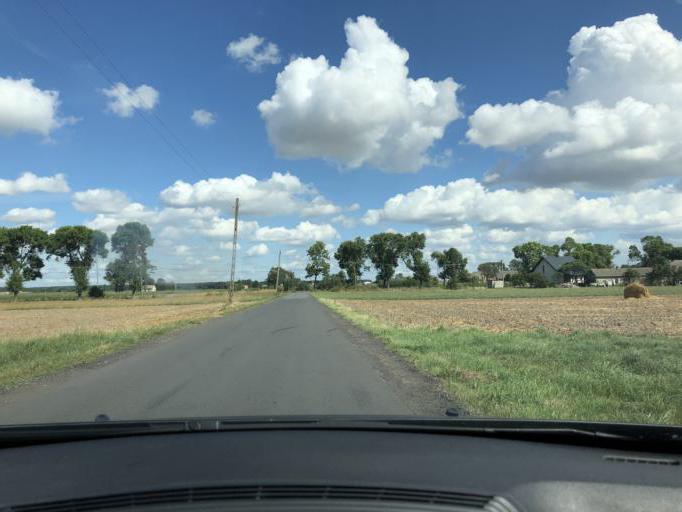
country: PL
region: Lodz Voivodeship
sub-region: Powiat wieruszowski
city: Czastary
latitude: 51.2407
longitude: 18.3589
